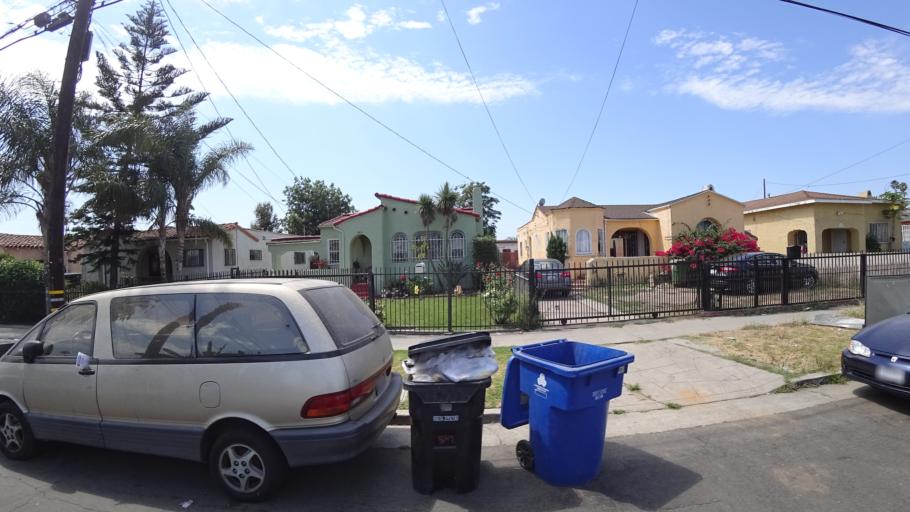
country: US
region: California
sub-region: Los Angeles County
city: Westmont
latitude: 33.9510
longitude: -118.2840
